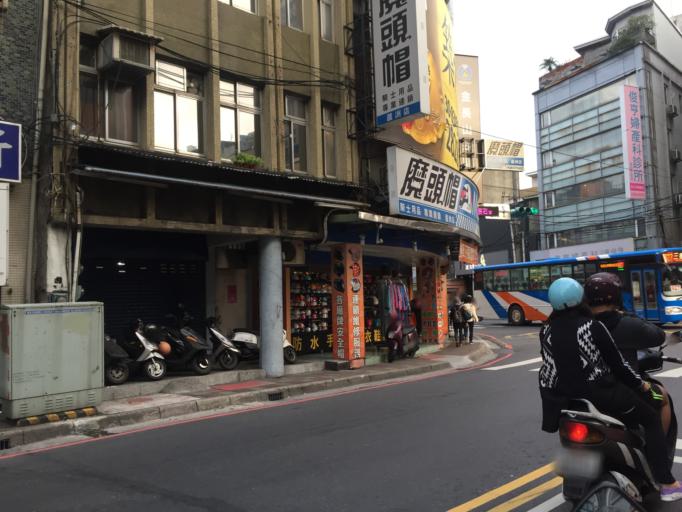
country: TW
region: Taipei
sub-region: Taipei
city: Banqiao
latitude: 25.0817
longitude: 121.4716
